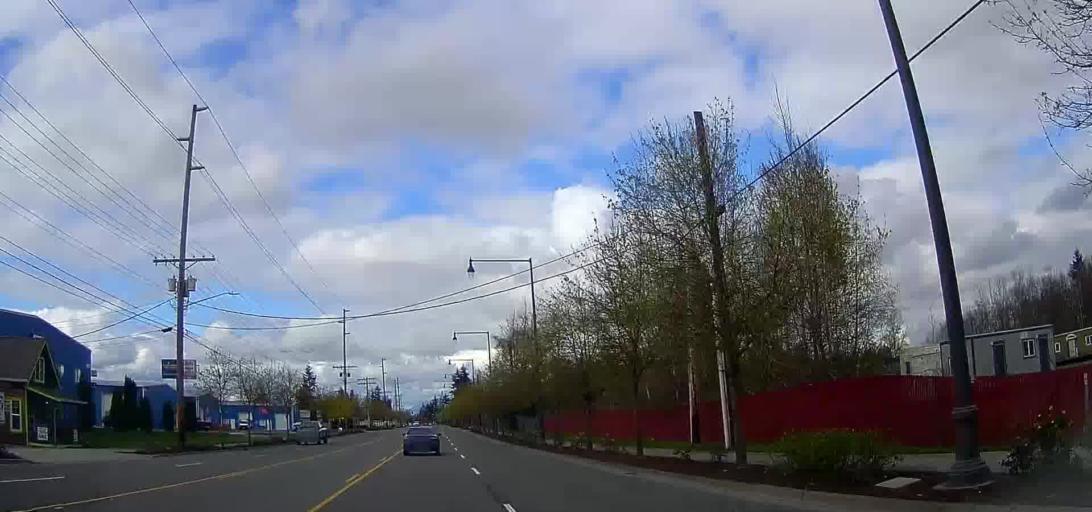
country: US
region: Washington
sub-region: Snohomish County
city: Smokey Point
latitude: 48.1271
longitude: -122.1837
